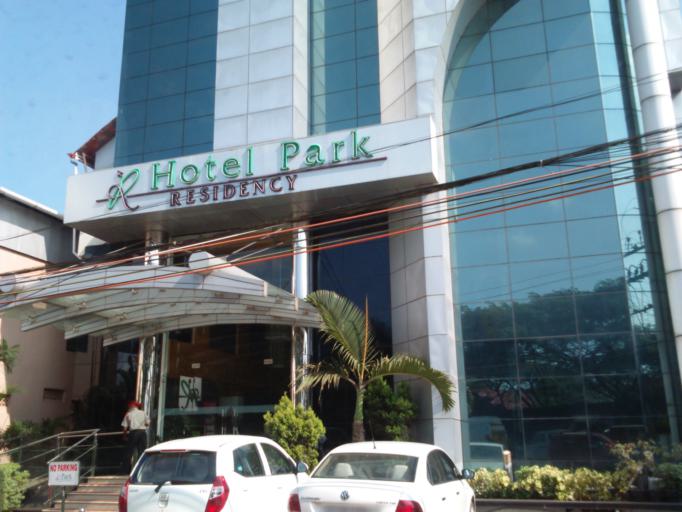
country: IN
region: Kerala
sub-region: Ernakulam
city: Elur
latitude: 10.0146
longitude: 76.3419
